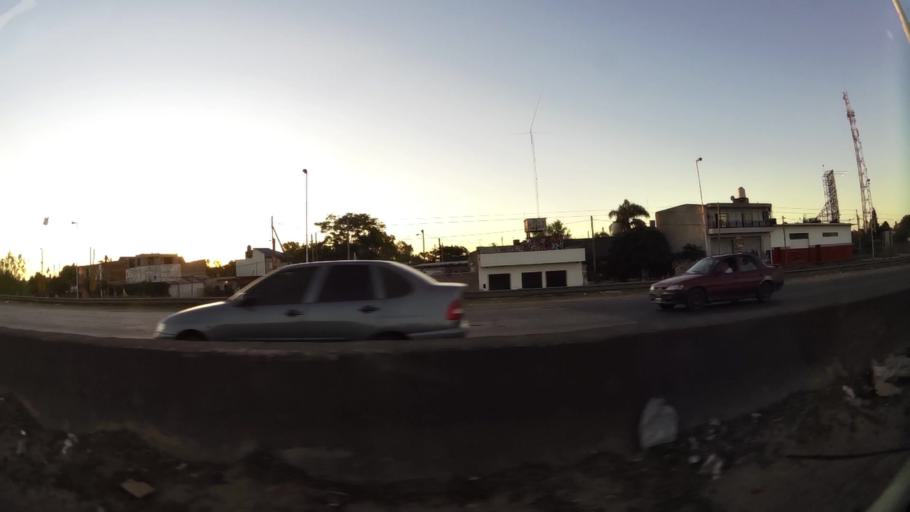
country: AR
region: Buenos Aires
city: Pontevedra
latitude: -34.7568
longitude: -58.6150
